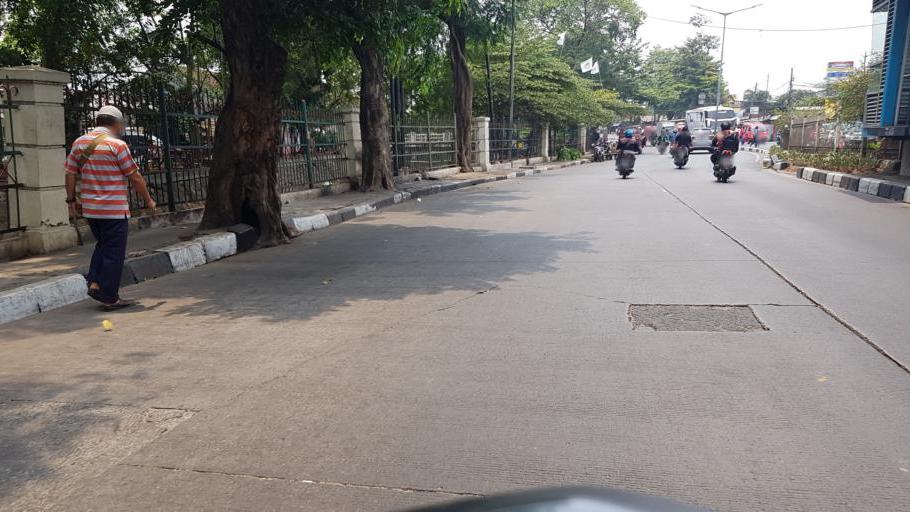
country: ID
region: Jakarta Raya
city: Jakarta
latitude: -6.2944
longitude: 106.8718
